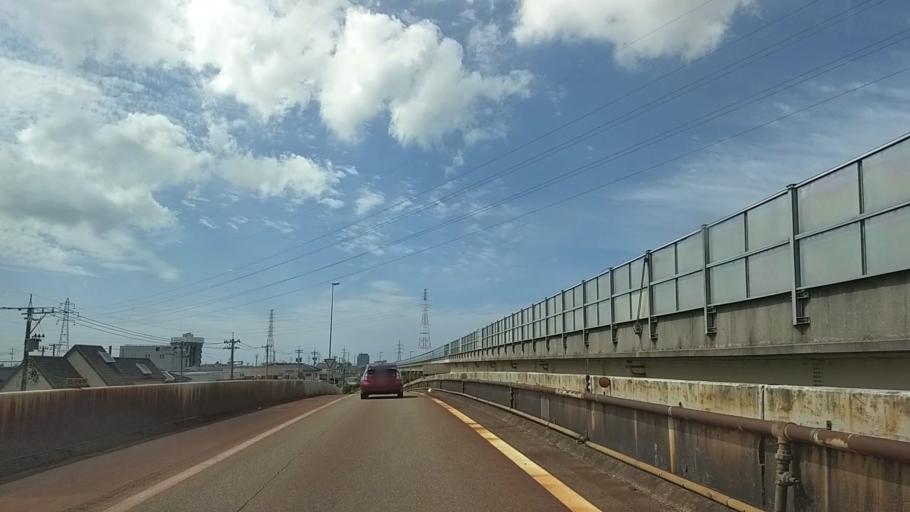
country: JP
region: Ishikawa
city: Kanazawa-shi
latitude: 36.6072
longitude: 136.6751
